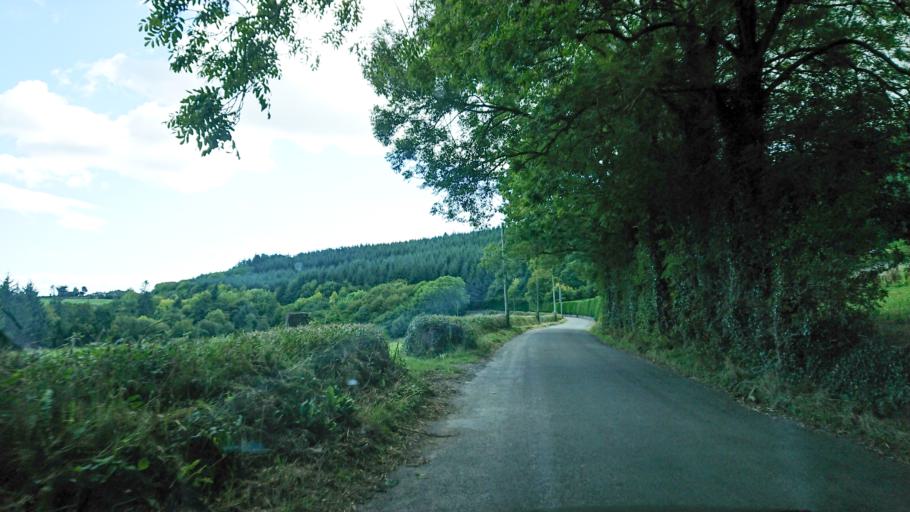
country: IE
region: Munster
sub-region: Waterford
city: Dungarvan
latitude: 52.1251
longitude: -7.6878
